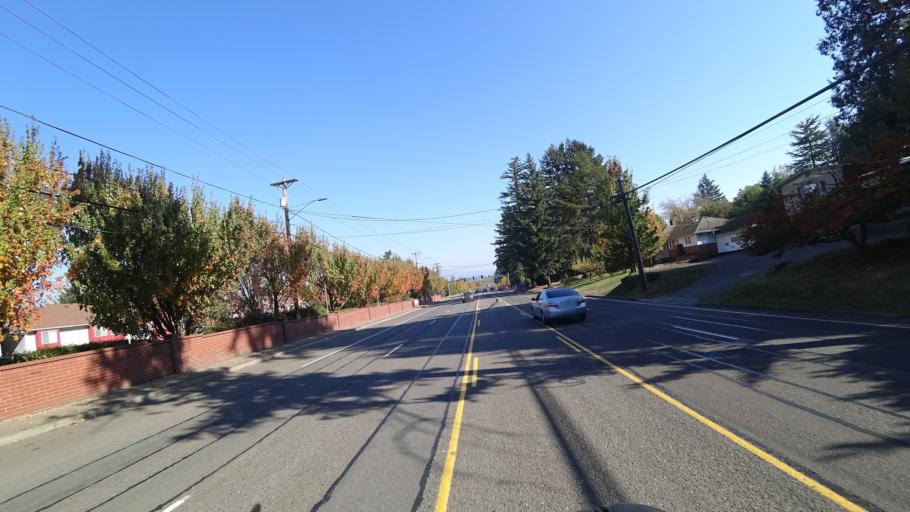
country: US
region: Oregon
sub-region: Multnomah County
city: Gresham
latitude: 45.5046
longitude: -122.4470
